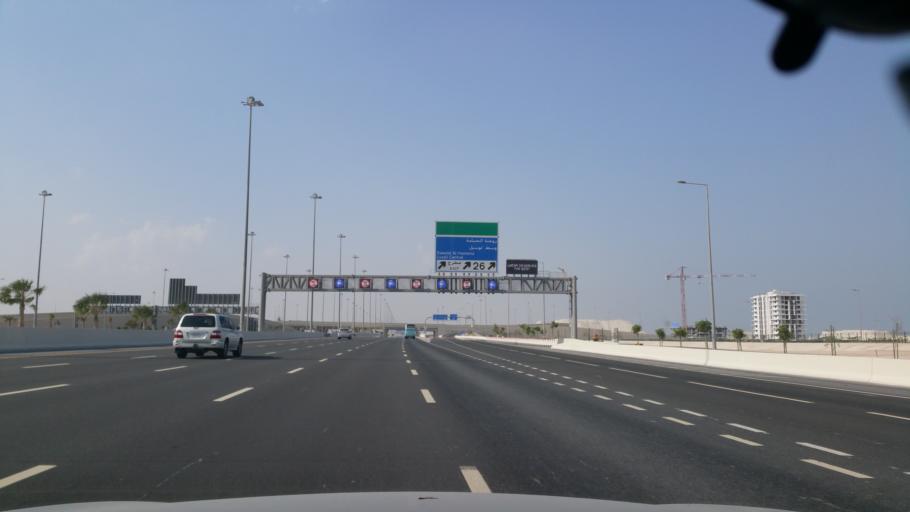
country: QA
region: Baladiyat Umm Salal
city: Umm Salal Muhammad
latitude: 25.4242
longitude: 51.4860
